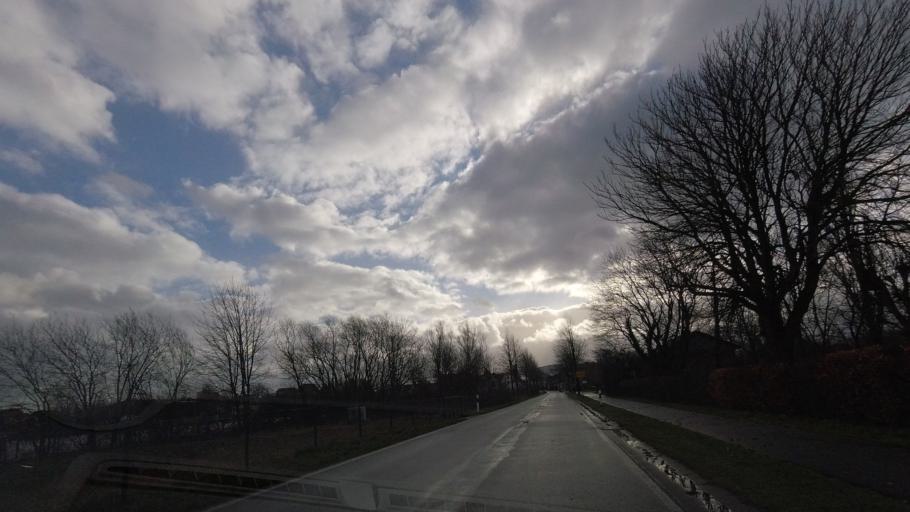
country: DE
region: Schleswig-Holstein
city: Grodersby
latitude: 54.6326
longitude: 9.9295
